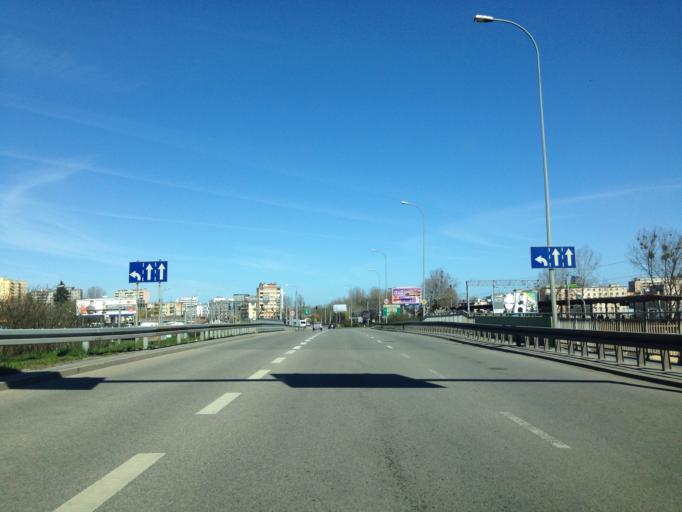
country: PL
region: Pomeranian Voivodeship
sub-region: Gdynia
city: Gdynia
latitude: 54.5061
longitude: 18.5344
